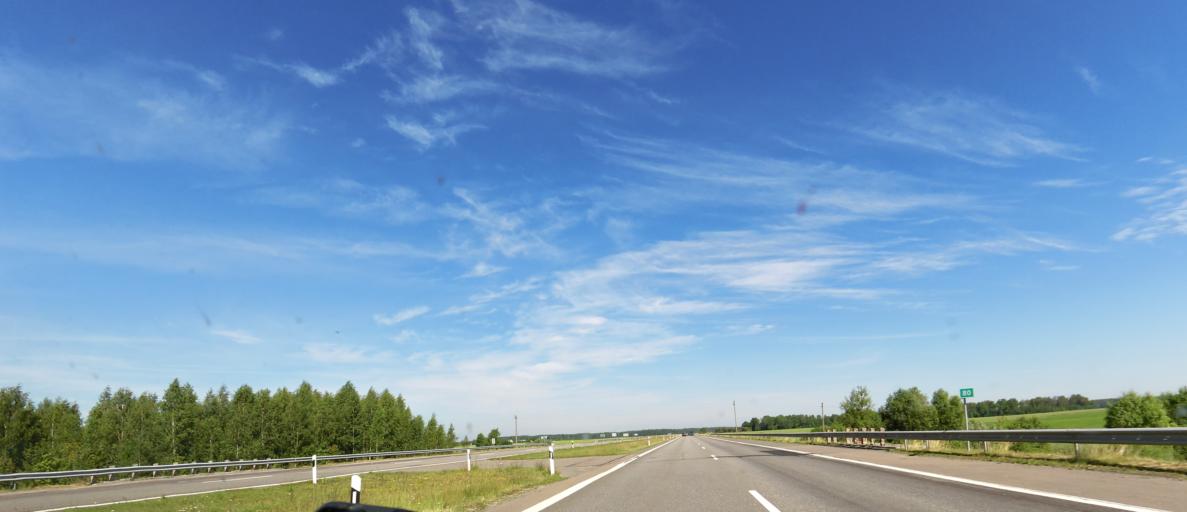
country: LT
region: Vilnius County
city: Ukmerge
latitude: 55.3142
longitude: 24.7829
